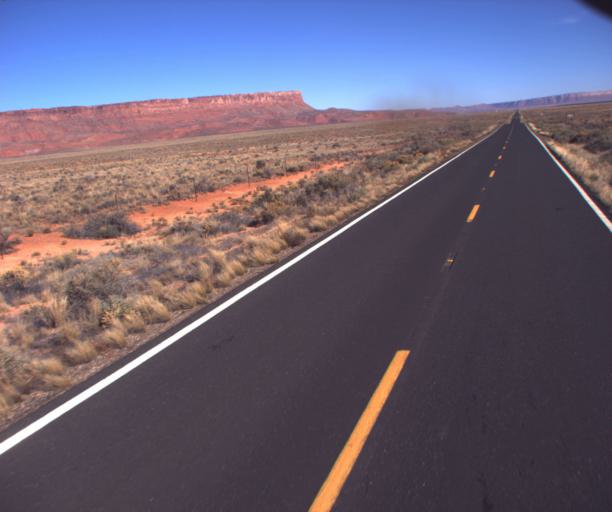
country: US
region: Arizona
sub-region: Coconino County
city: Page
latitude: 36.7054
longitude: -111.9494
